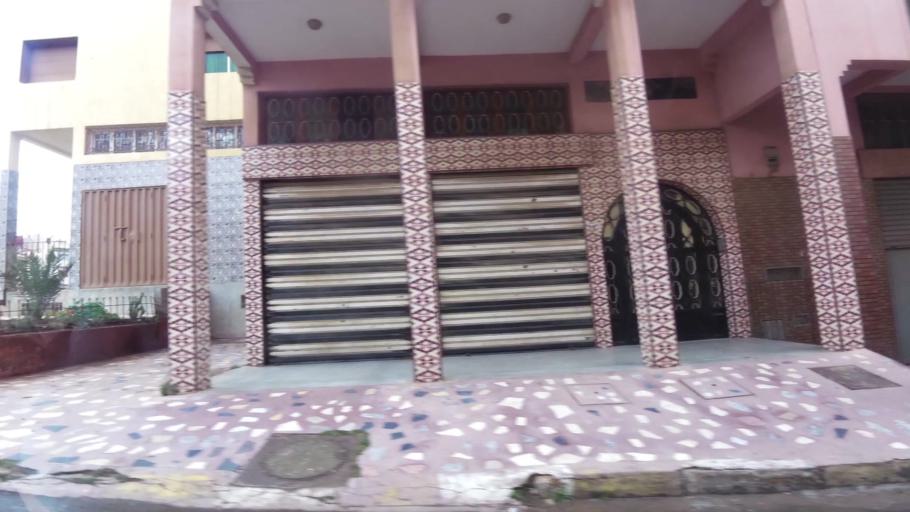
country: MA
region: Grand Casablanca
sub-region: Nouaceur
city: Bouskoura
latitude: 33.5059
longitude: -7.6527
